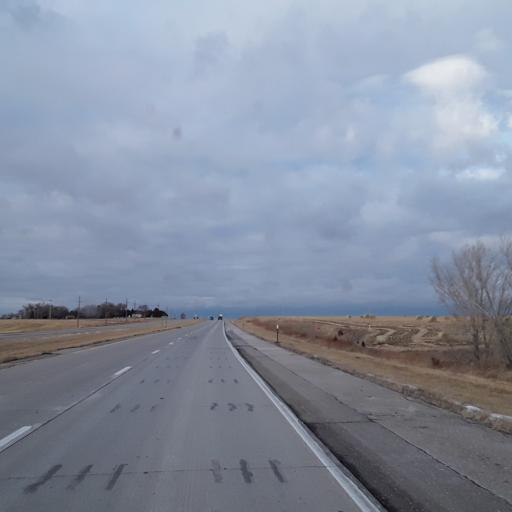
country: US
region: Nebraska
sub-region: Thayer County
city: Hebron
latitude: 40.2597
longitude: -97.5765
